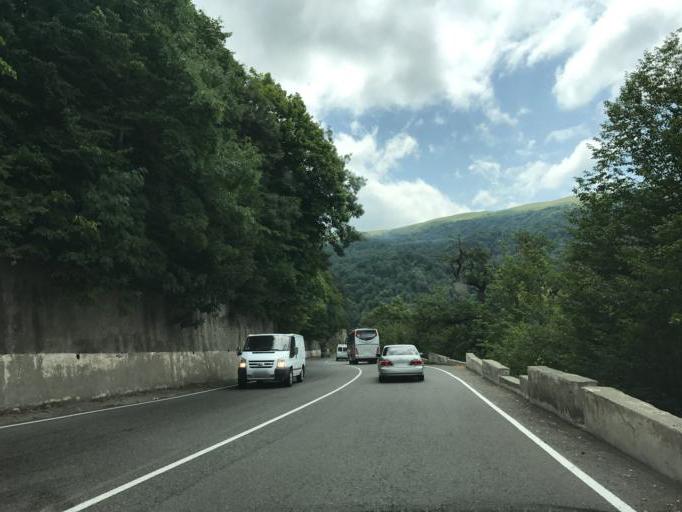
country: AM
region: Tavush
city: Dilijan
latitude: 40.6919
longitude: 44.8598
